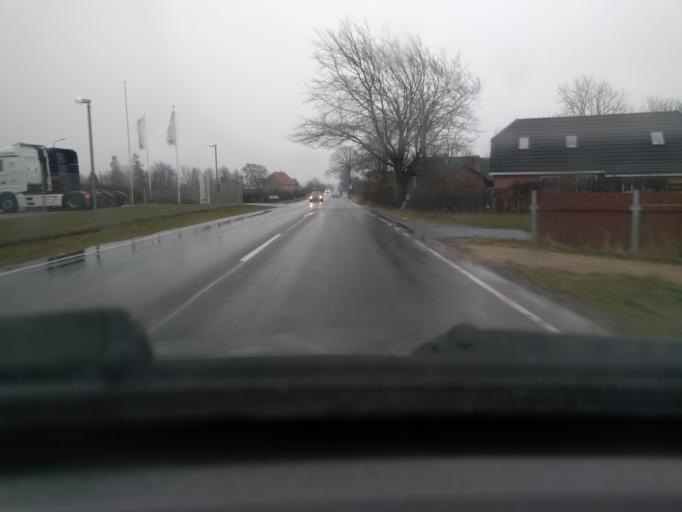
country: DK
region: Central Jutland
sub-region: Silkeborg Kommune
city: Kjellerup
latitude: 56.2691
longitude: 9.4388
